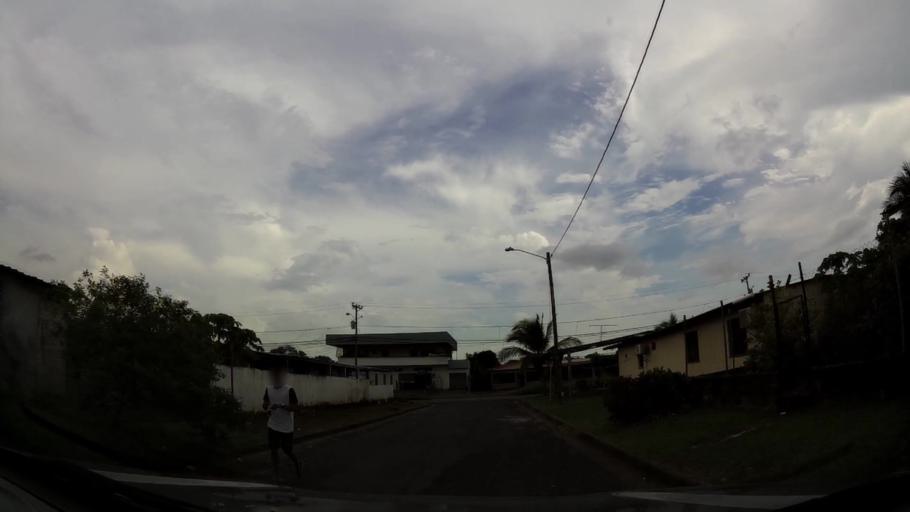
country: PA
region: Panama
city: Cabra Numero Uno
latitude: 9.0911
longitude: -79.3440
